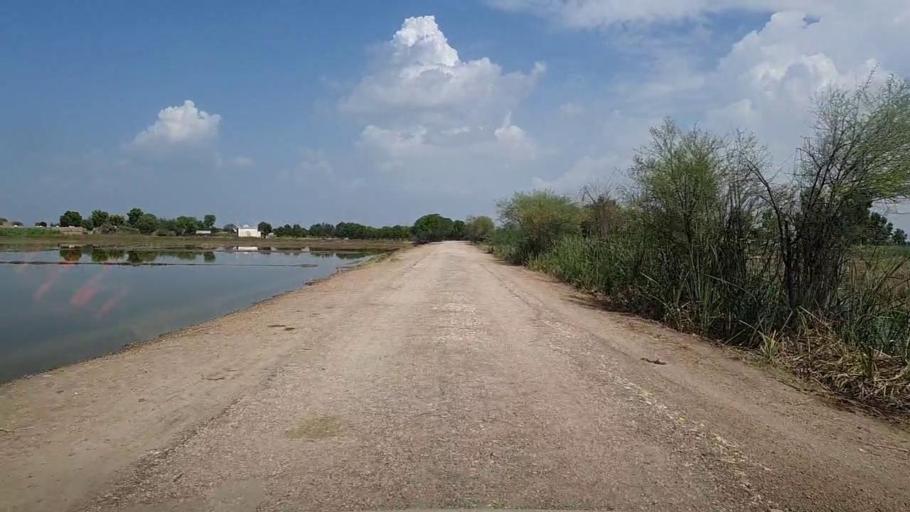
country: PK
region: Sindh
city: Bhiria
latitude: 26.9190
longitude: 68.2285
